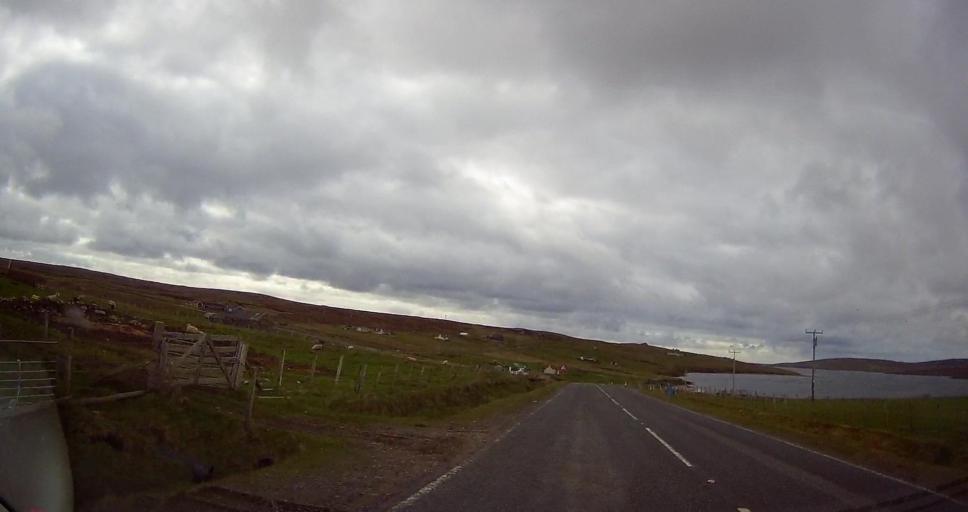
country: GB
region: Scotland
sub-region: Shetland Islands
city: Shetland
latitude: 60.6632
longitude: -1.0534
